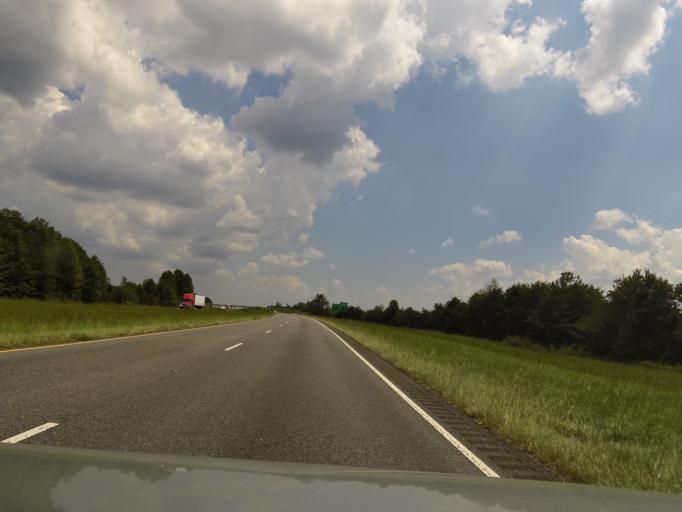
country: US
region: North Carolina
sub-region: Polk County
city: Columbus
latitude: 35.2879
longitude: -82.0762
